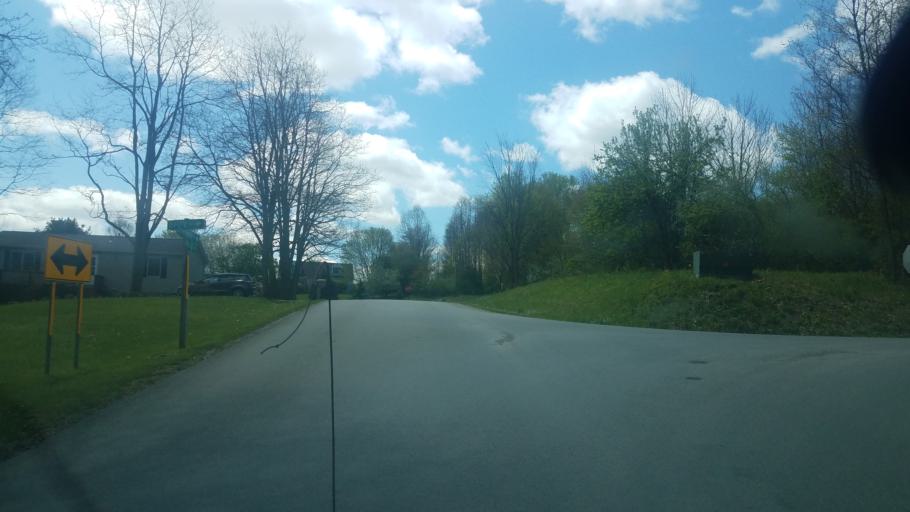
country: US
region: Ohio
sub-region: Knox County
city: Gambier
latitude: 40.4351
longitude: -82.3612
